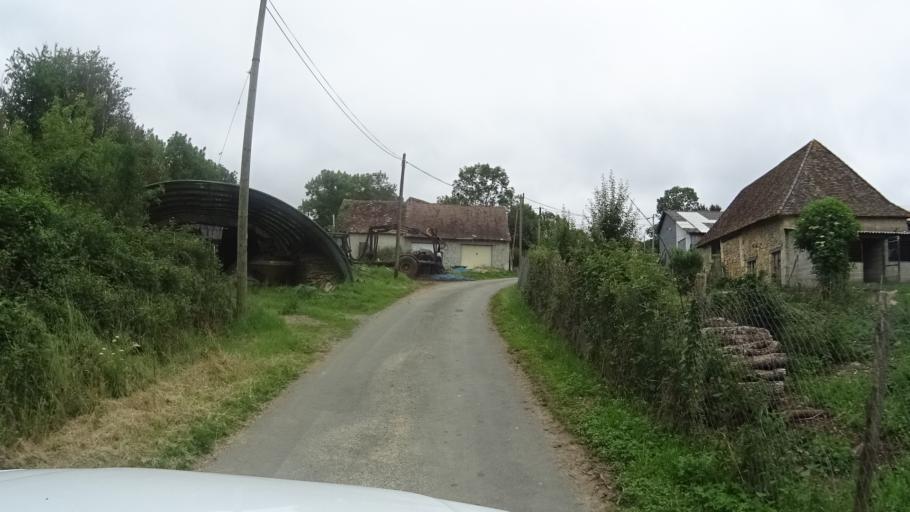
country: FR
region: Aquitaine
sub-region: Departement de la Dordogne
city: Lembras
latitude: 44.9230
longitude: 0.4782
